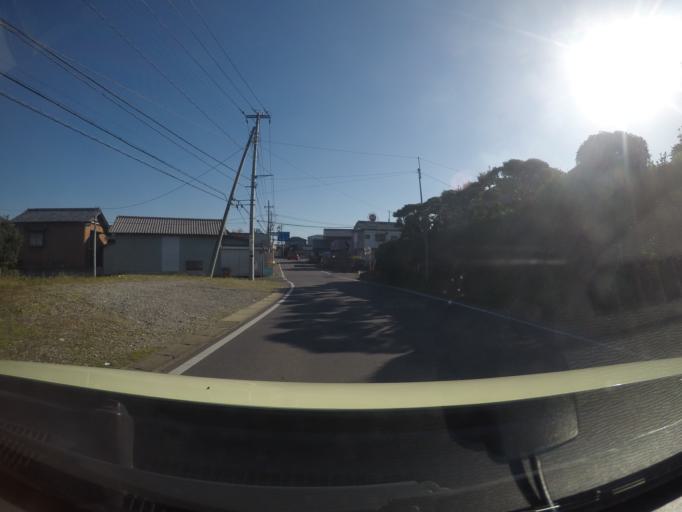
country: JP
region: Ibaraki
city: Naka
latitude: 36.0903
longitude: 140.1269
